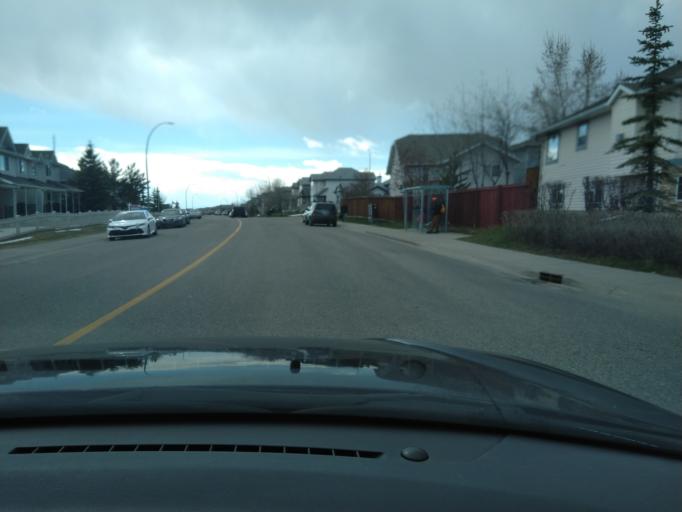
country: CA
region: Alberta
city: Calgary
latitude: 51.1340
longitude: -114.2133
